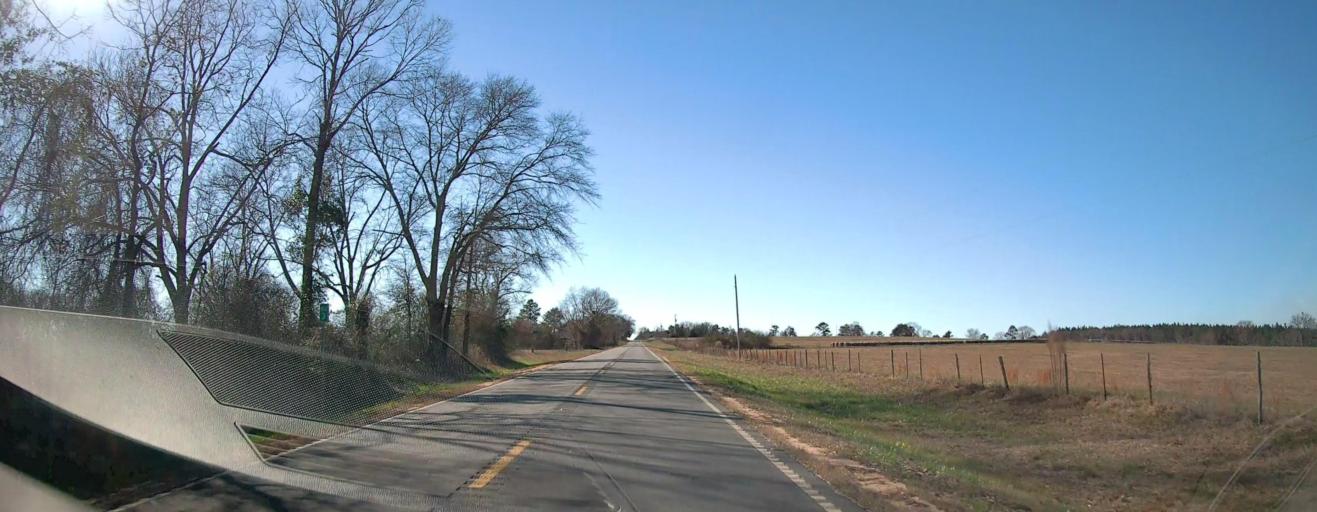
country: US
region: Georgia
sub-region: Taylor County
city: Butler
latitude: 32.6595
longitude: -84.3330
